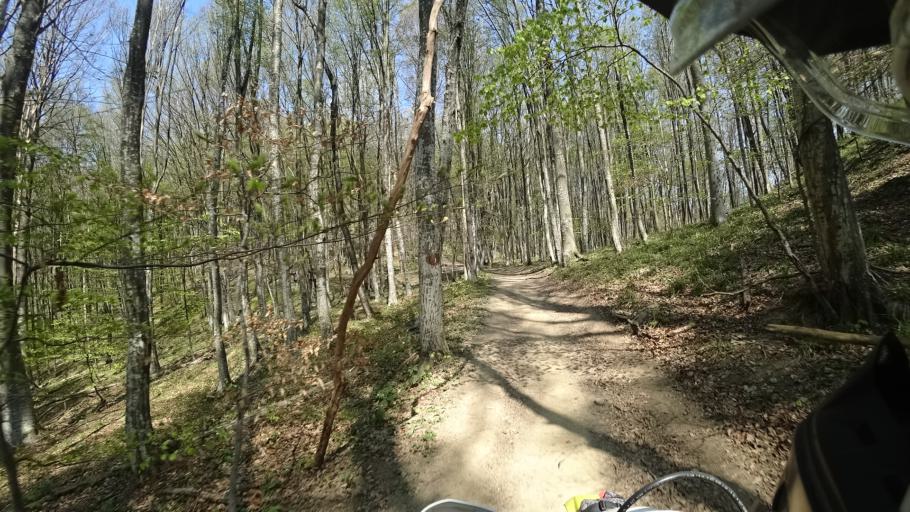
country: HR
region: Zagrebacka
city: Jablanovec
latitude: 45.8844
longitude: 15.9119
